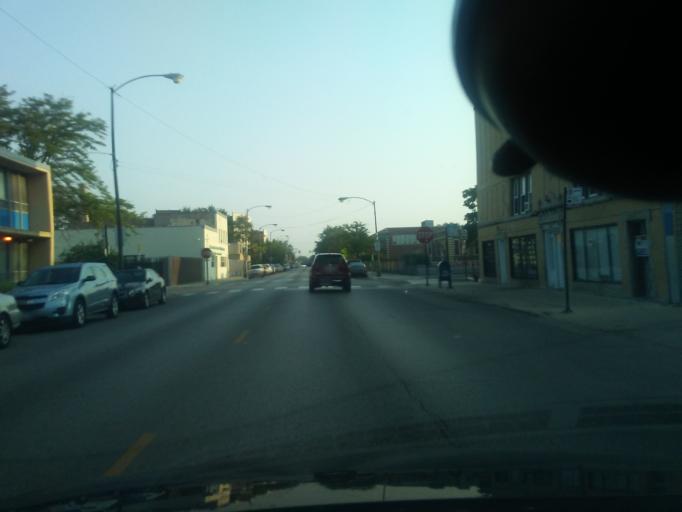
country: US
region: Illinois
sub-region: Cook County
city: Lincolnwood
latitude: 41.9919
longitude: -87.6994
